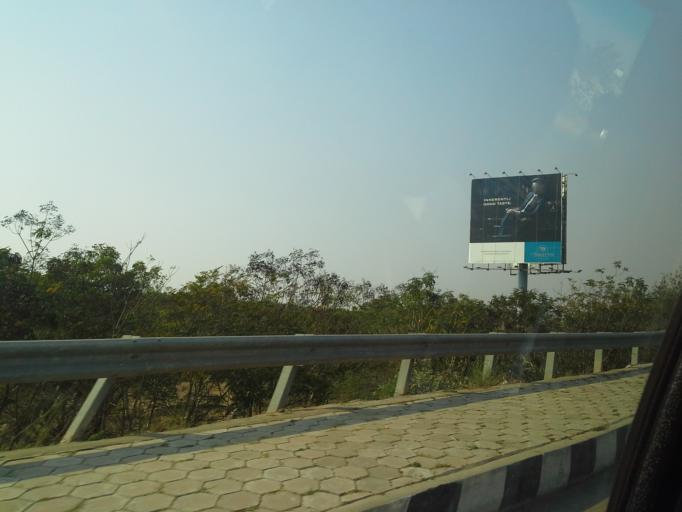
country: IN
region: Telangana
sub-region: Rangareddi
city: Sriramnagar
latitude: 17.2469
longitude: 78.3829
